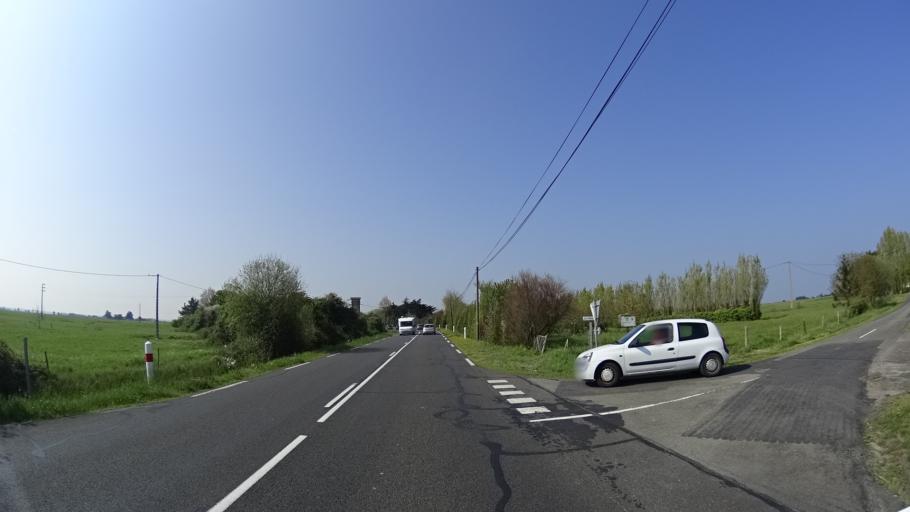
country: FR
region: Pays de la Loire
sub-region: Departement de la Vendee
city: Bouin
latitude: 46.9859
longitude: -1.9811
